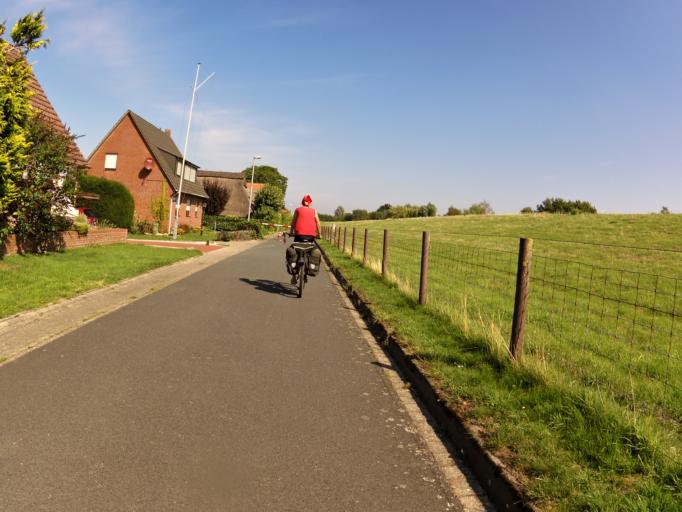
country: DE
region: Lower Saxony
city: Elsfleth
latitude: 53.2583
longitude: 8.4759
